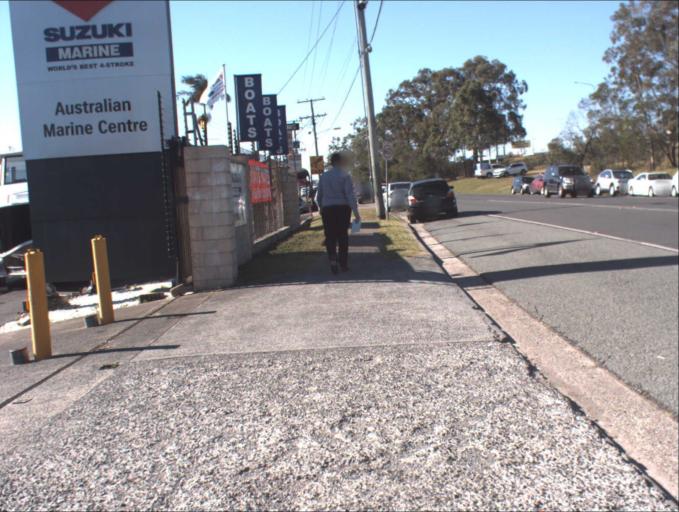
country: AU
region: Queensland
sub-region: Logan
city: Springwood
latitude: -27.6333
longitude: 153.1315
